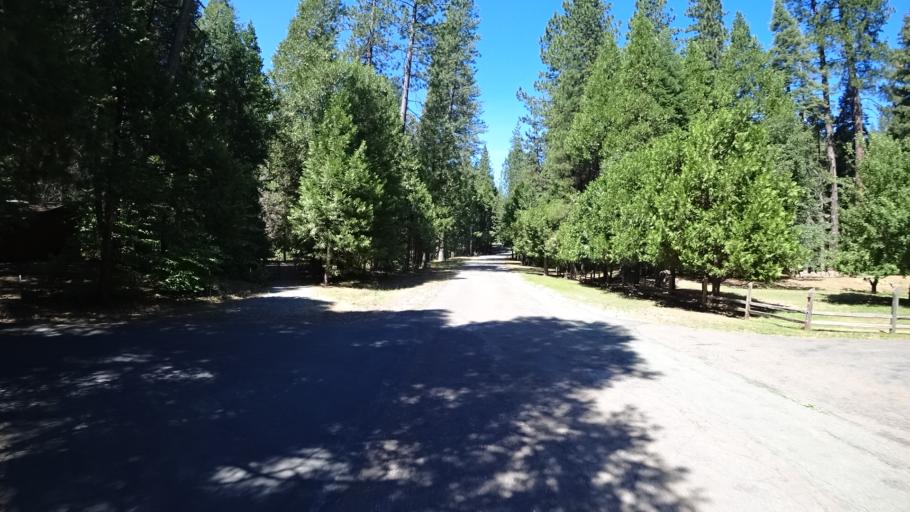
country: US
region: California
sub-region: Amador County
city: Pioneer
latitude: 38.4391
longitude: -120.4305
